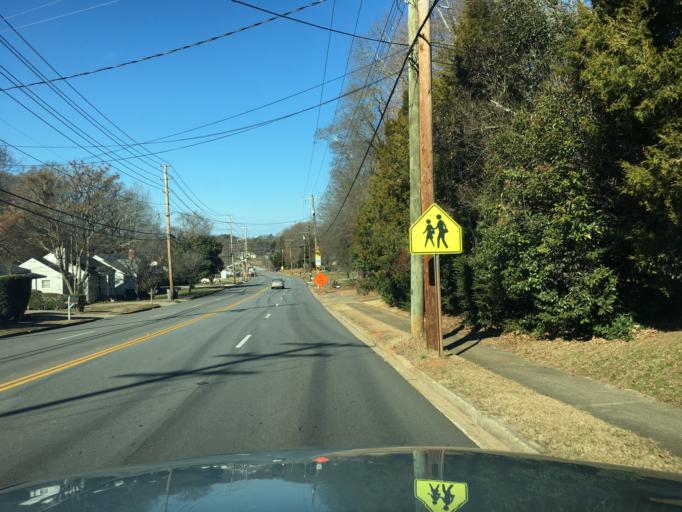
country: US
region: South Carolina
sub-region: Greenville County
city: Sans Souci
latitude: 34.8917
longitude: -82.4203
